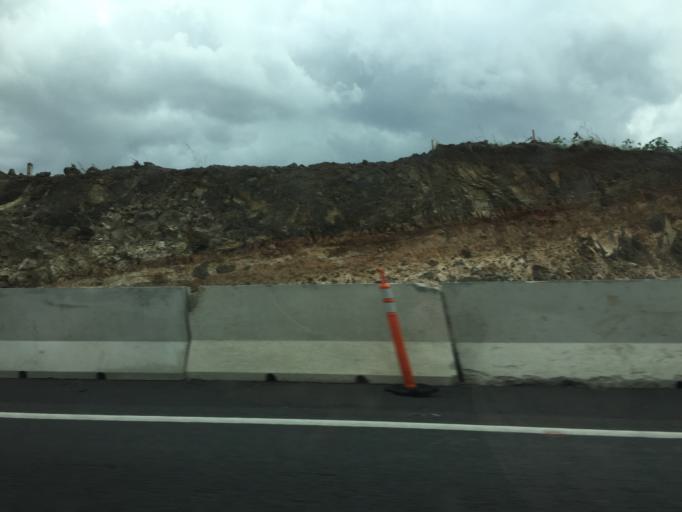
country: MX
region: Jalisco
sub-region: Zapotlanejo
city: La Mezquitera
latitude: 20.5852
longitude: -103.0981
